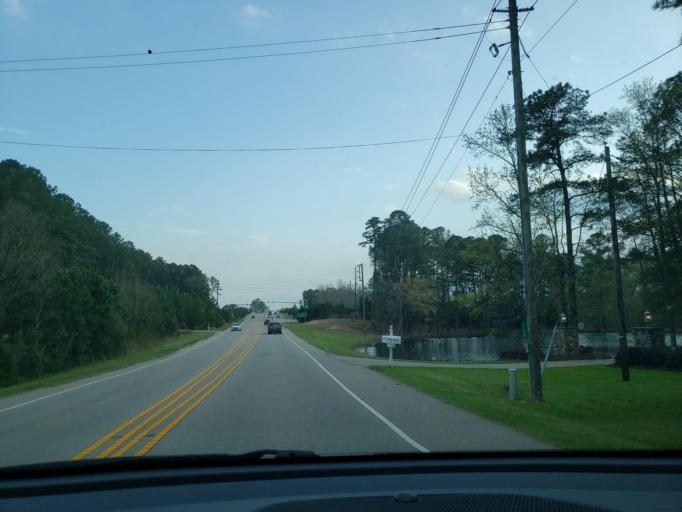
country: US
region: North Carolina
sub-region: Wake County
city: Green Level
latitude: 35.7506
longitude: -78.8945
